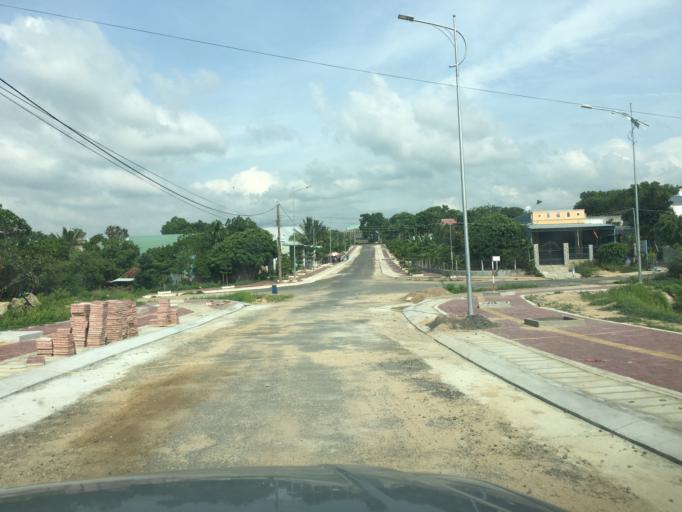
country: VN
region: Gia Lai
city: Kong Chro
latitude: 13.7734
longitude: 108.5271
